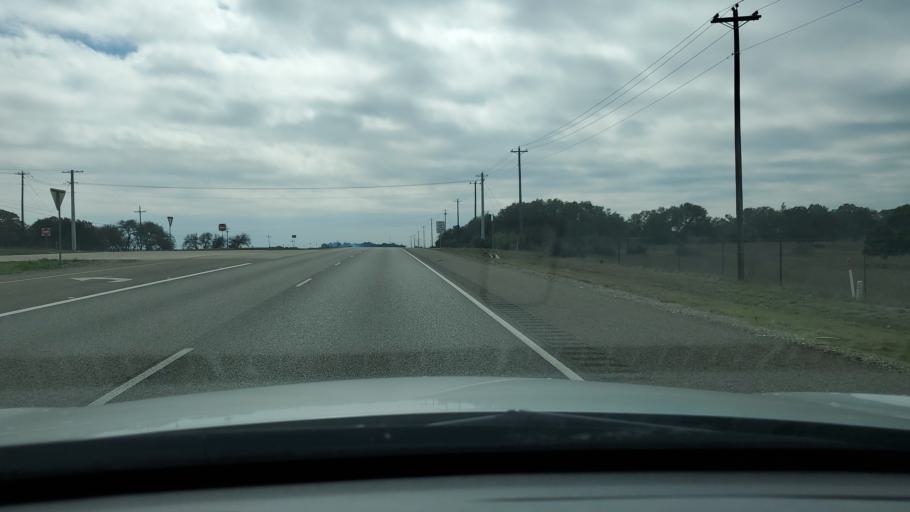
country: US
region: Texas
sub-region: Williamson County
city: Florence
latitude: 30.8079
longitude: -97.7716
